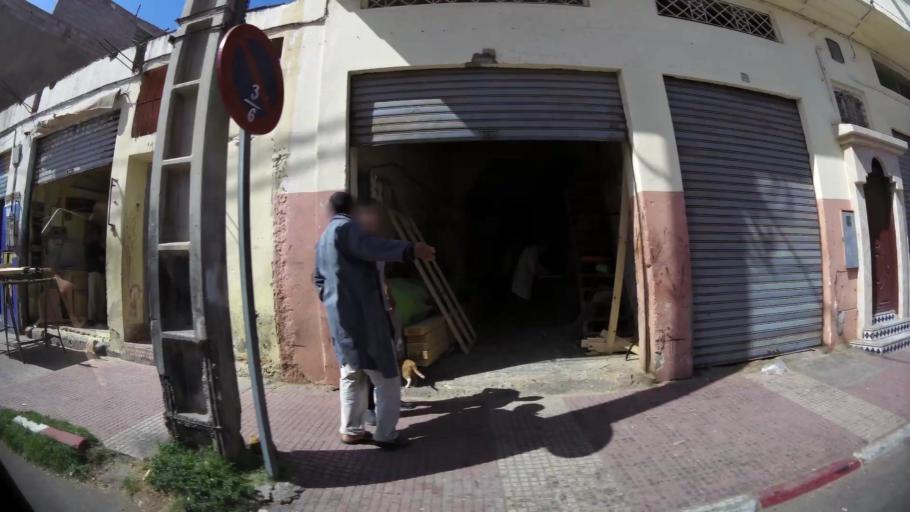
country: MA
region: Souss-Massa-Draa
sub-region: Inezgane-Ait Mellou
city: Inezgane
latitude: 30.3539
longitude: -9.5365
